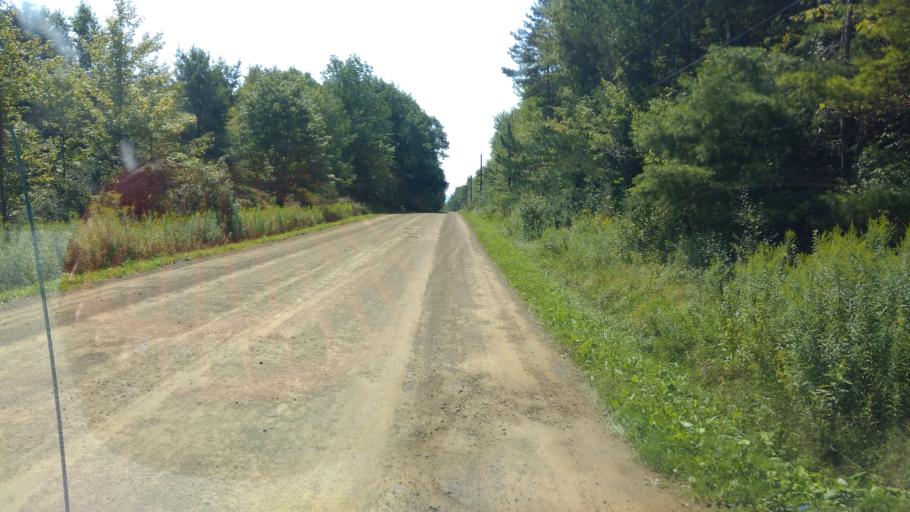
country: US
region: New York
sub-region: Allegany County
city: Belmont
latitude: 42.3534
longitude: -78.0413
